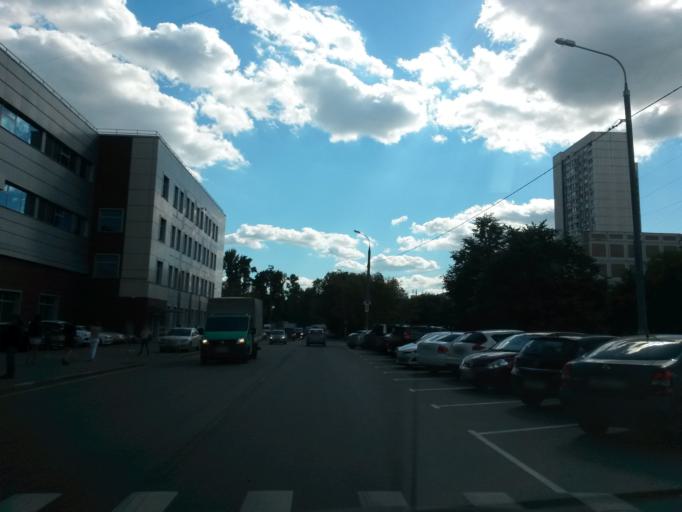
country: RU
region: Moskovskaya
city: Kozhukhovo
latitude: 55.7021
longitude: 37.6884
